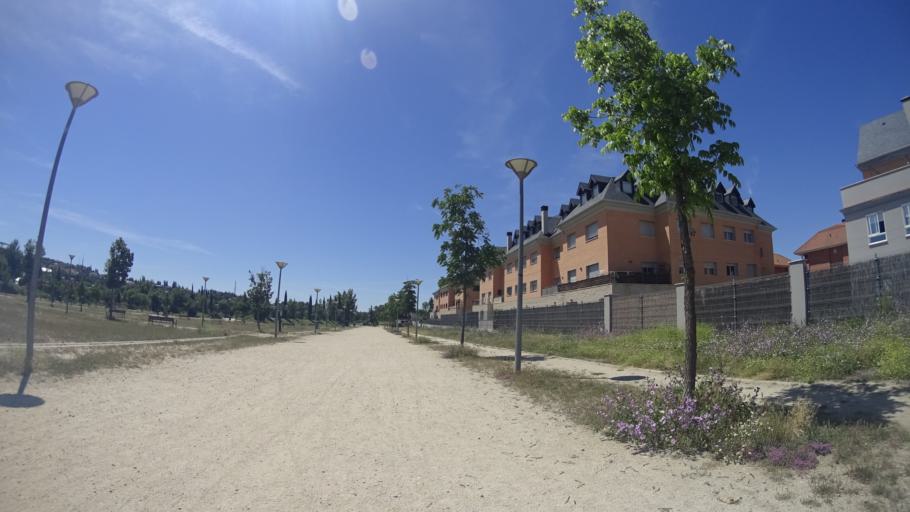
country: ES
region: Madrid
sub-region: Provincia de Madrid
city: Collado-Villalba
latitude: 40.6428
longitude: -4.0070
